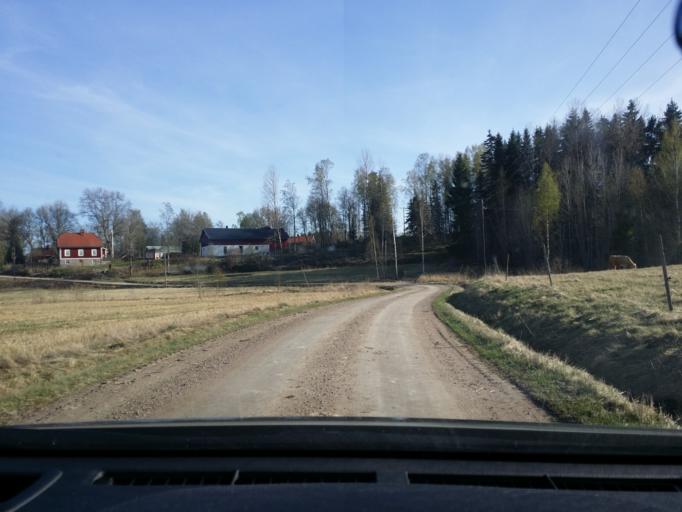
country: SE
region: Dalarna
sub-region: Avesta Kommun
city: Avesta
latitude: 60.0726
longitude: 16.3682
